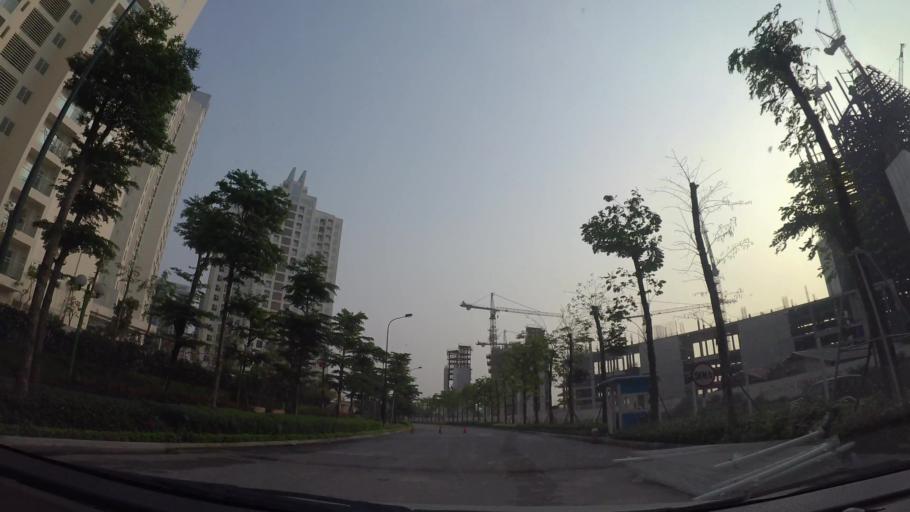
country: VN
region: Ha Noi
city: Tay Ho
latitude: 21.0832
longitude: 105.7918
